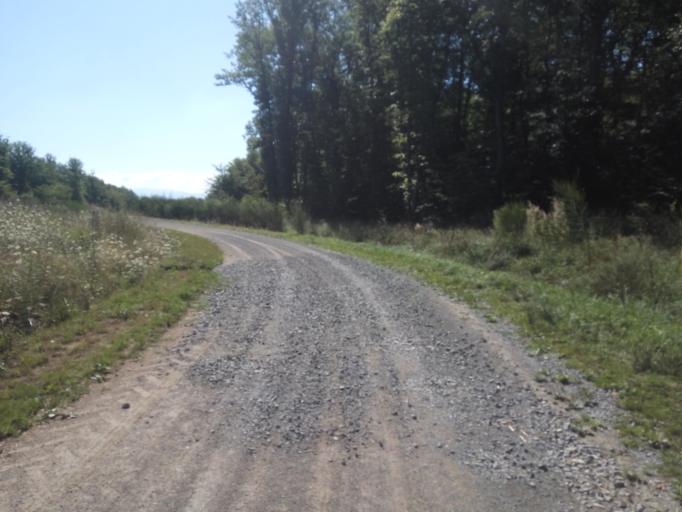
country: FR
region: Auvergne
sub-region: Departement de l'Allier
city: Brugheas
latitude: 46.0871
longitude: 3.3526
